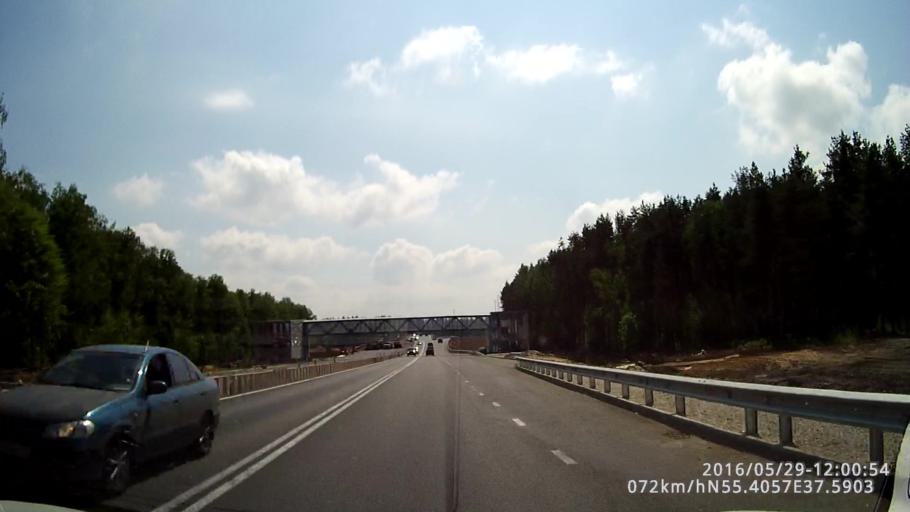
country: RU
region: Moskovskaya
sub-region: Podol'skiy Rayon
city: Podol'sk
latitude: 55.4054
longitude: 37.5906
